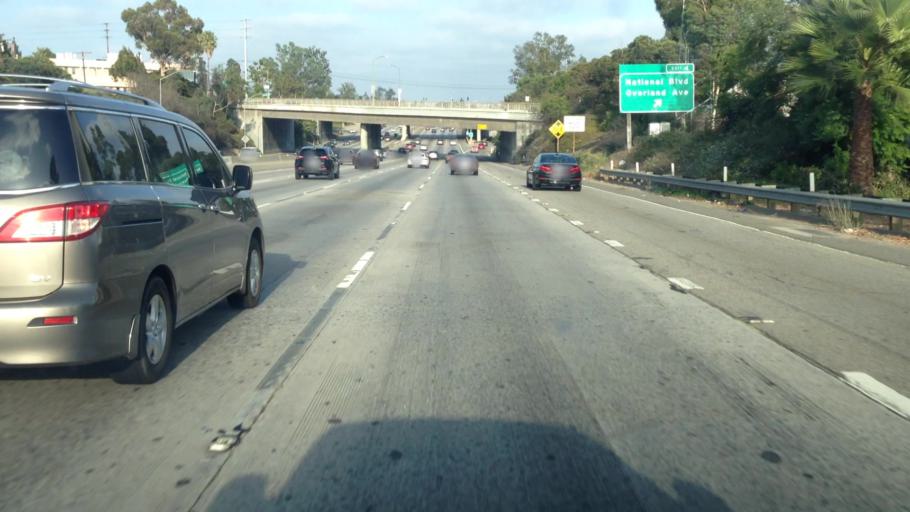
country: US
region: California
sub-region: Los Angeles County
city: Century City
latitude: 34.0316
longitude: -118.4209
